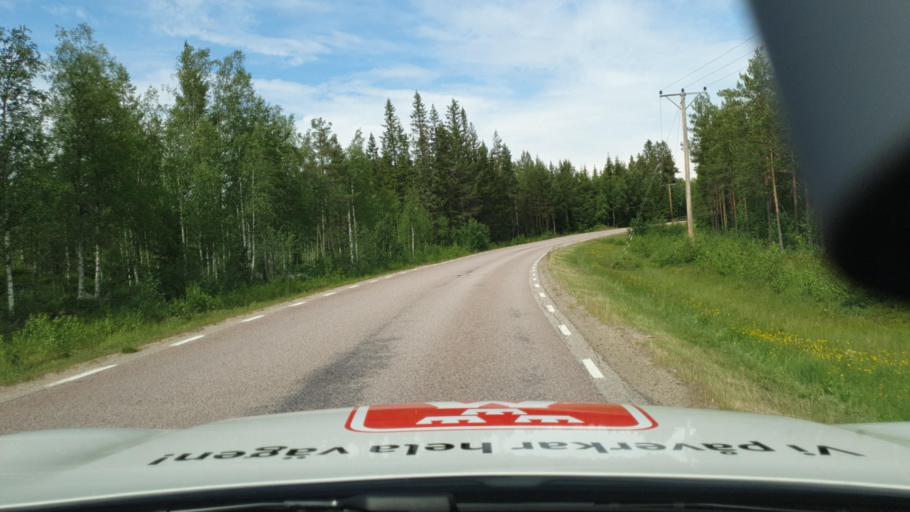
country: NO
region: Hedmark
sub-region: Asnes
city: Flisa
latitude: 60.7158
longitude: 12.6150
